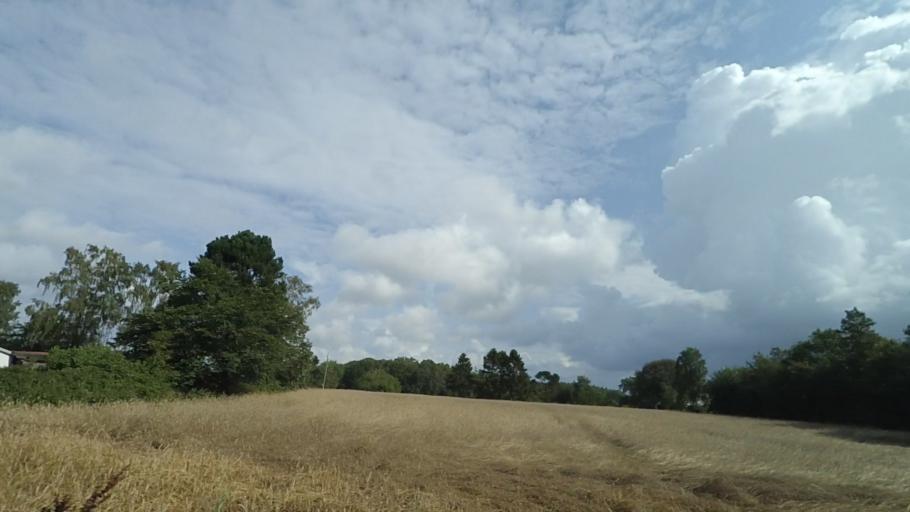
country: DK
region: Central Jutland
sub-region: Syddjurs Kommune
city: Ryomgard
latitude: 56.4619
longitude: 10.5282
